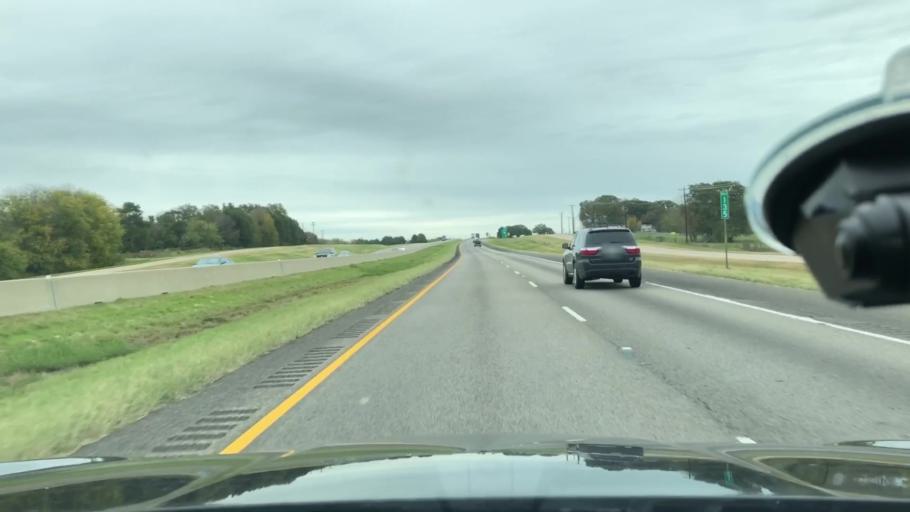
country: US
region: Texas
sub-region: Hopkins County
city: Sulphur Springs
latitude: 33.1521
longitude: -95.4354
